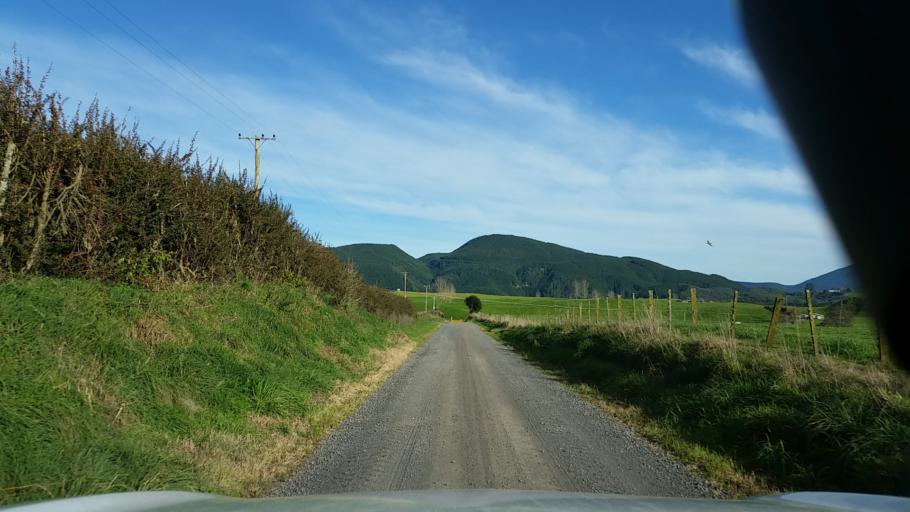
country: NZ
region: Waikato
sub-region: South Waikato District
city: Tokoroa
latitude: -38.3650
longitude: 176.0579
